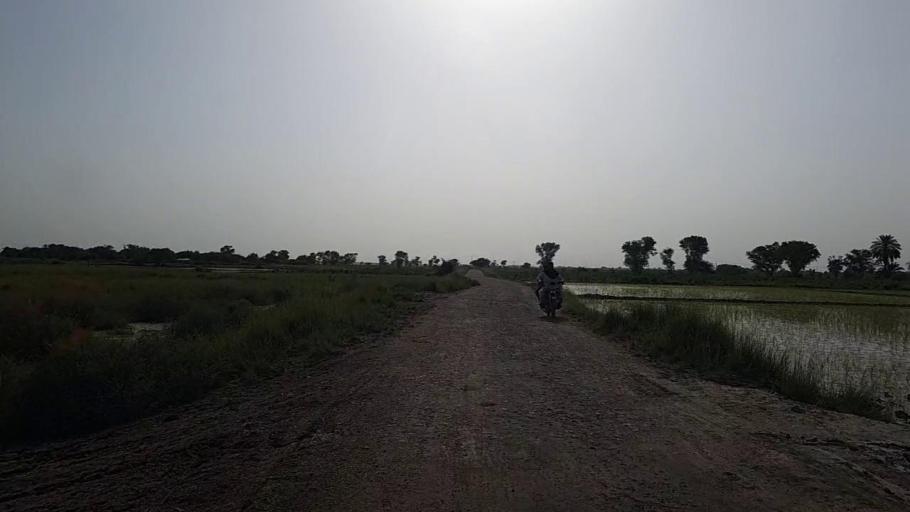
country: PK
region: Sindh
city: Pad Idan
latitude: 26.8531
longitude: 68.3087
